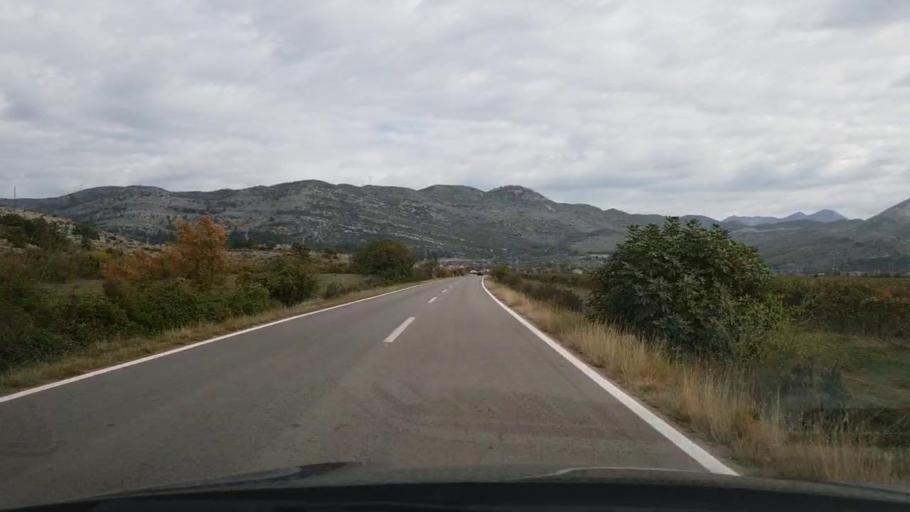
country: BA
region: Republika Srpska
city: Trebinje
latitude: 42.6861
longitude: 18.3154
